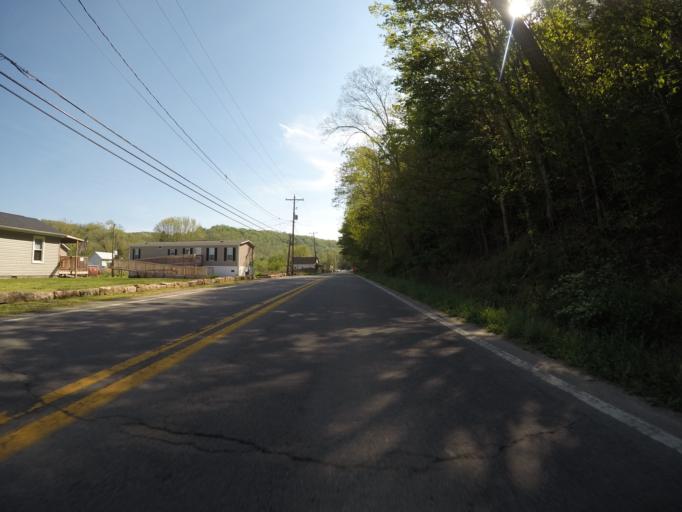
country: US
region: West Virginia
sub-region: Kanawha County
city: Clendenin
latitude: 38.4704
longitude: -81.4006
